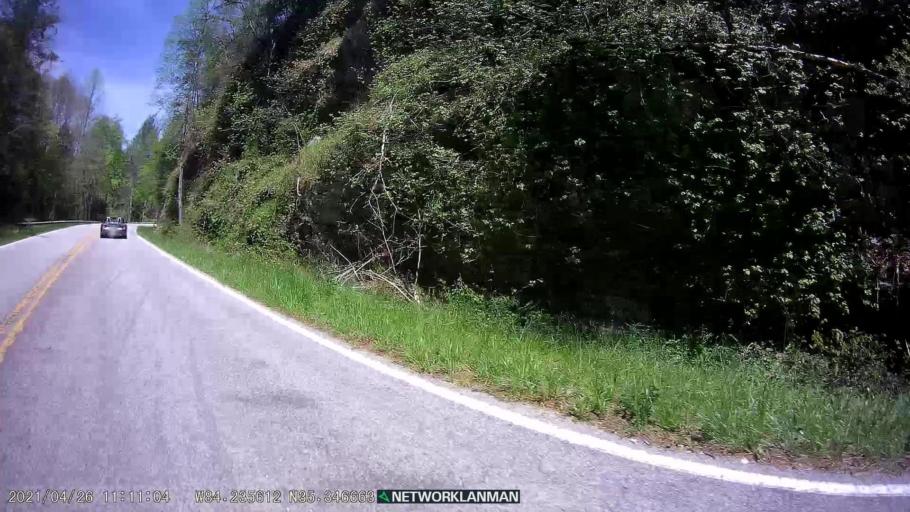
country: US
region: Tennessee
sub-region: Monroe County
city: Madisonville
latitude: 35.3467
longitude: -84.2355
